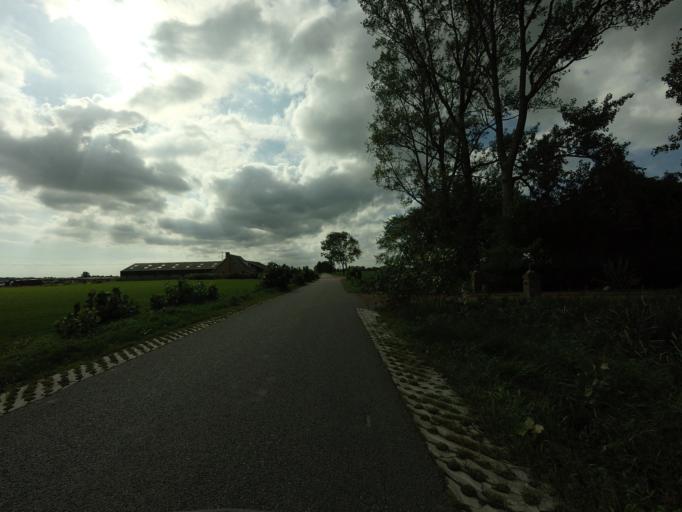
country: NL
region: Friesland
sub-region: Gemeente Littenseradiel
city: Wommels
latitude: 53.0701
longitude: 5.5895
